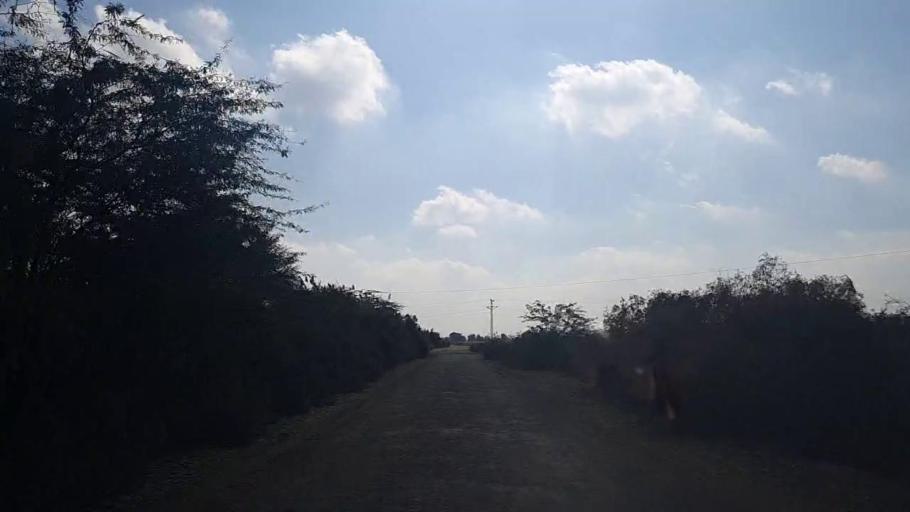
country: PK
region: Sindh
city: Sanghar
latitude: 26.0610
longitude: 69.0271
